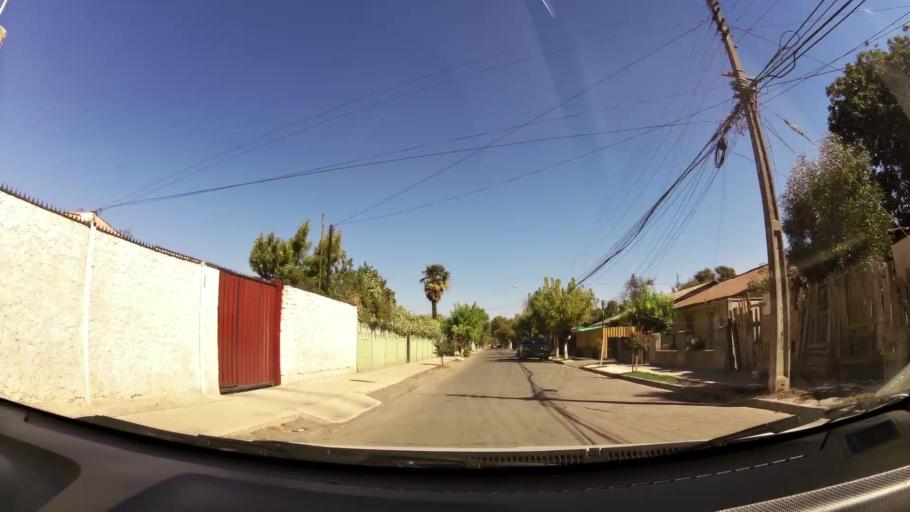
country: CL
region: O'Higgins
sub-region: Provincia de Cachapoal
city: Rancagua
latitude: -34.1703
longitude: -70.7018
